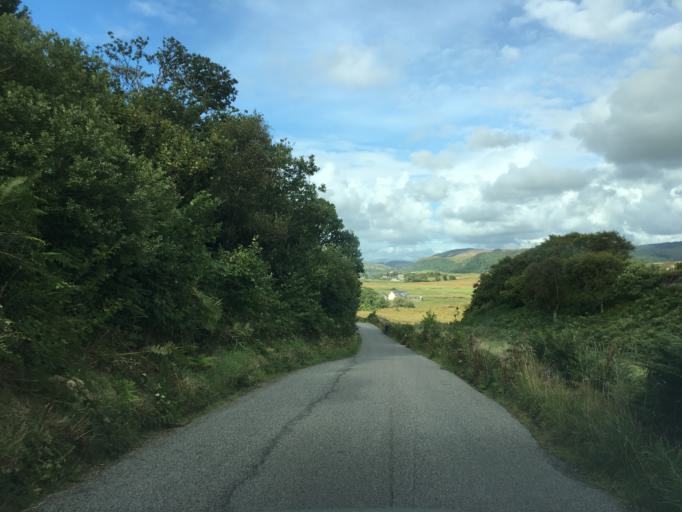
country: GB
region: Scotland
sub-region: Argyll and Bute
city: Oban
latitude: 56.2811
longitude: -5.6216
